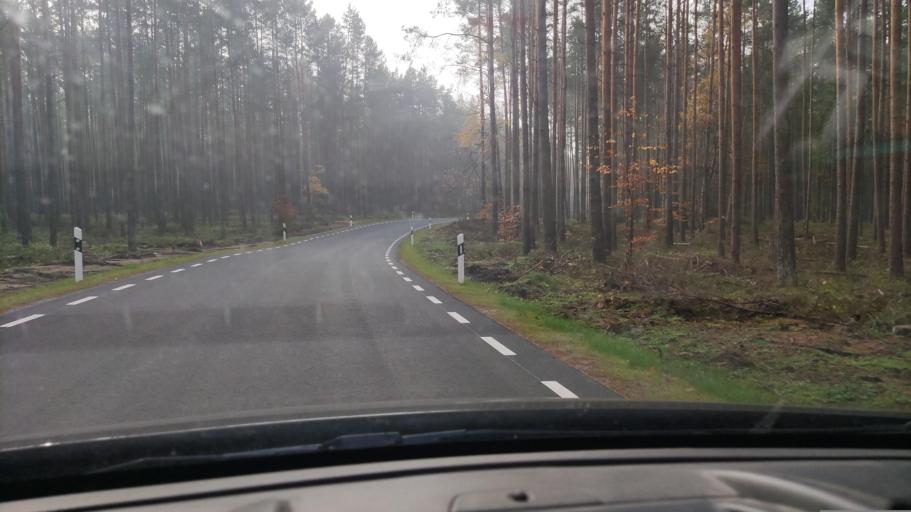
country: DE
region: Brandenburg
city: Furstenberg
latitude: 53.2428
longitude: 13.0897
